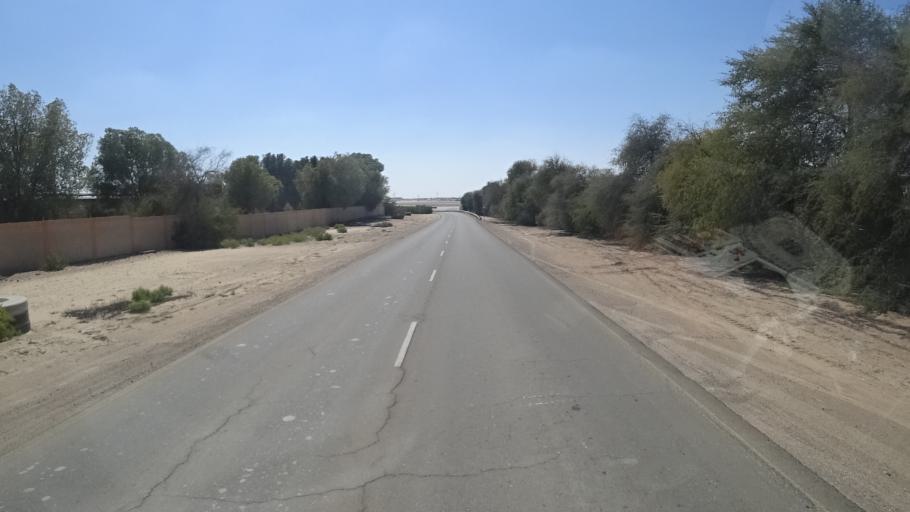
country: AE
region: Abu Dhabi
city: Abu Dhabi
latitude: 24.1995
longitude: 54.7030
